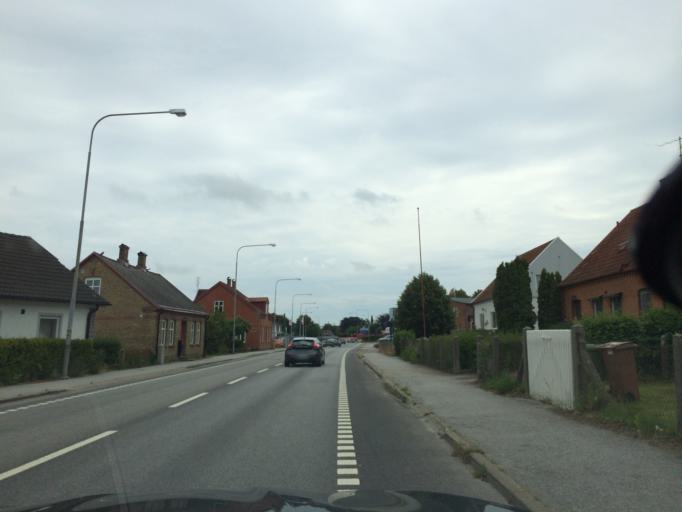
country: SE
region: Skane
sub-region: Tomelilla Kommun
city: Tomelilla
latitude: 55.5486
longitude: 13.9441
